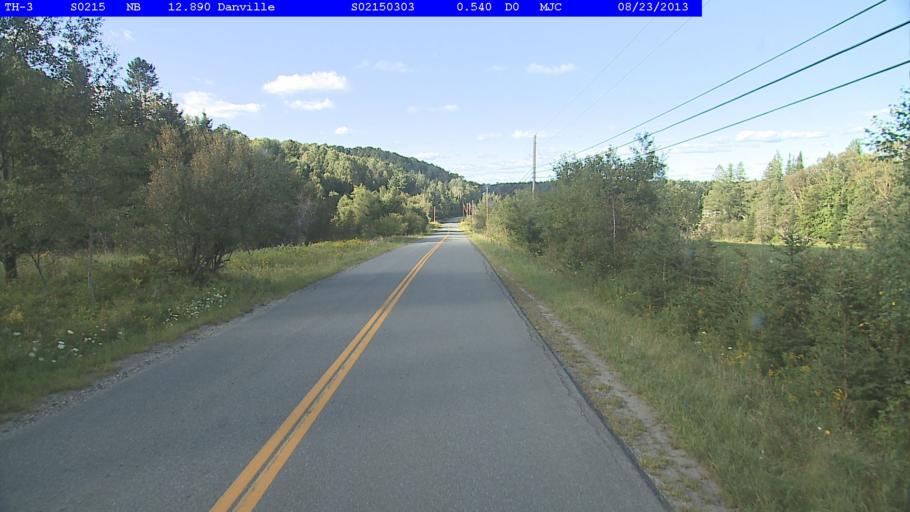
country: US
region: Vermont
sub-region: Caledonia County
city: Saint Johnsbury
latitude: 44.3735
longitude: -72.1456
